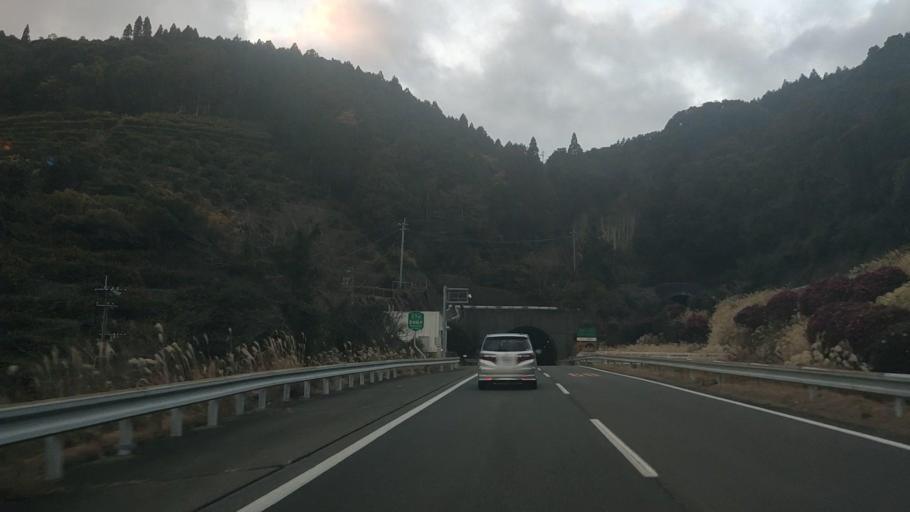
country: JP
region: Nagasaki
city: Obita
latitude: 32.8123
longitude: 129.9316
